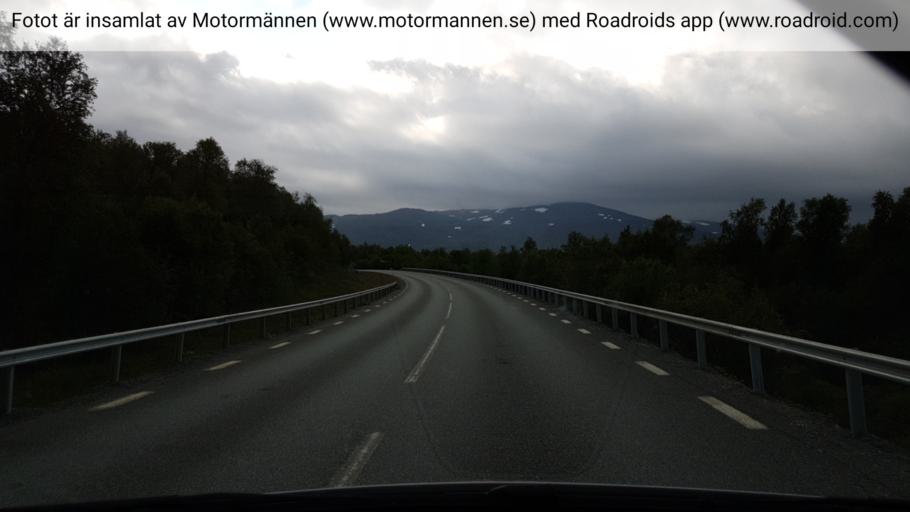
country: NO
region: Nordland
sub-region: Rana
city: Mo i Rana
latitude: 66.0587
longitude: 14.8728
